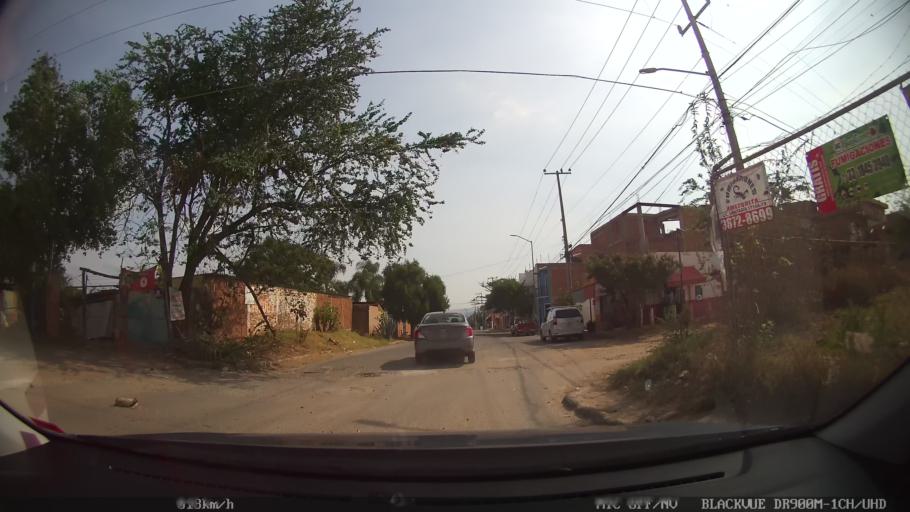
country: MX
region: Jalisco
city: Tonala
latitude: 20.6351
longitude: -103.2362
